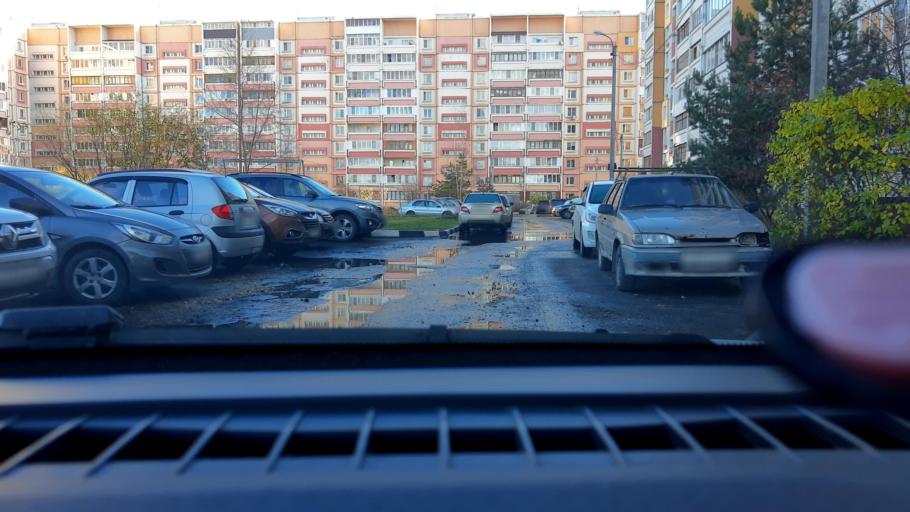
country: RU
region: Nizjnij Novgorod
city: Gorbatovka
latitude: 56.3691
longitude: 43.8078
